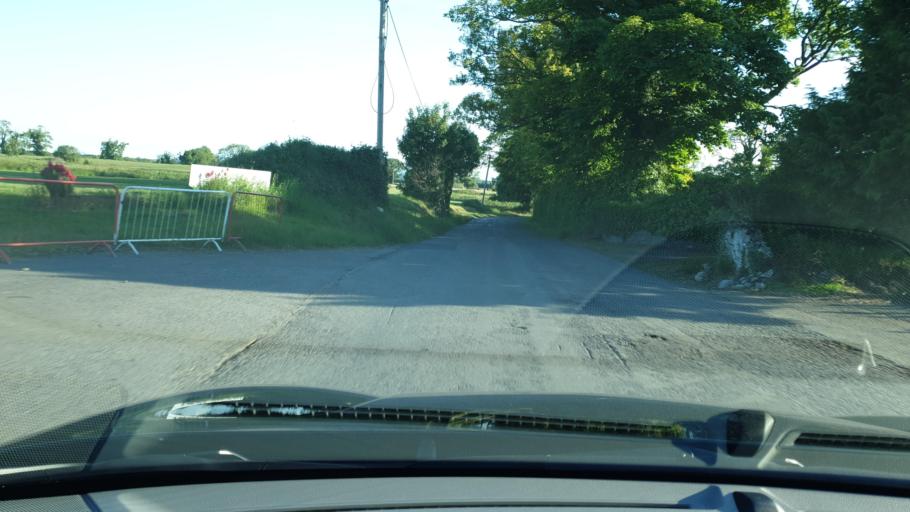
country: IE
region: Leinster
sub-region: Fingal County
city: Swords
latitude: 53.5059
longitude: -6.2383
